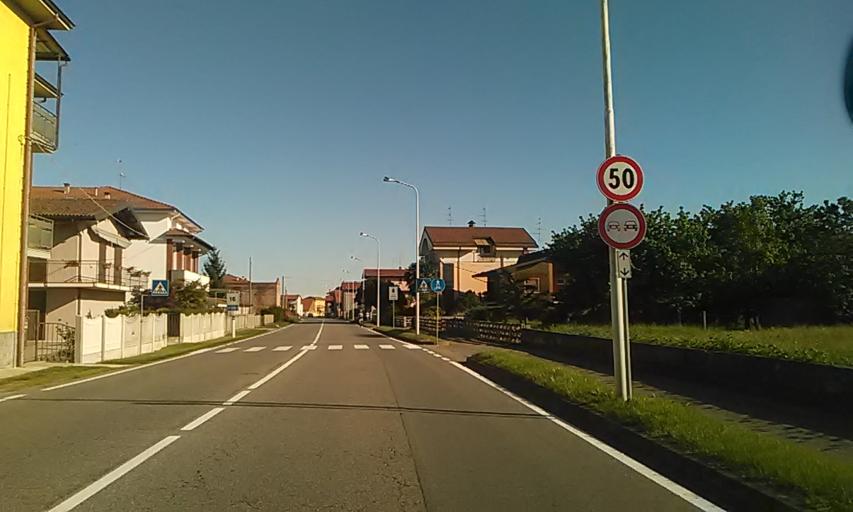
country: IT
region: Piedmont
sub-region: Provincia di Novara
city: Momo
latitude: 45.5805
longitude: 8.5515
